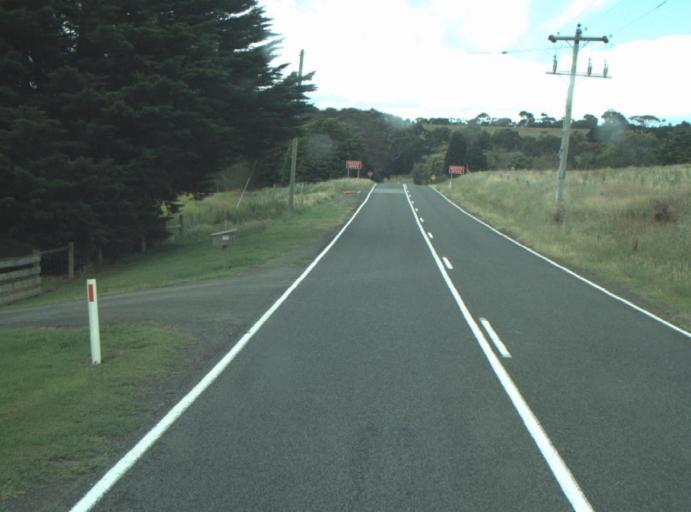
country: AU
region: Victoria
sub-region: Greater Geelong
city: Wandana Heights
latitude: -38.2046
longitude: 144.2711
